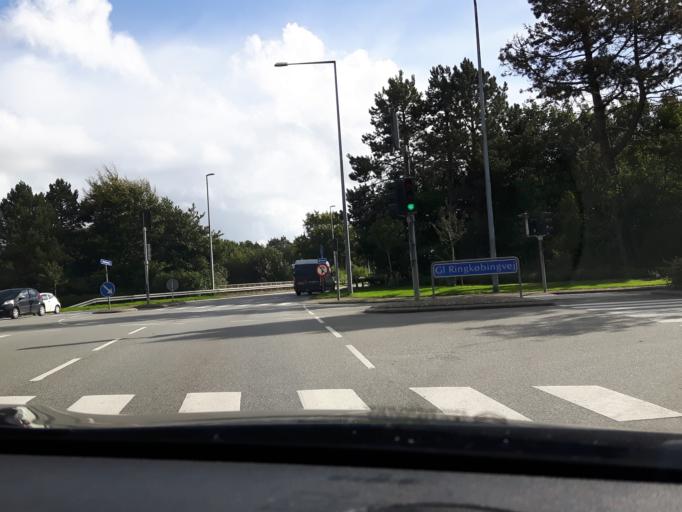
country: DK
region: Central Jutland
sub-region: Herning Kommune
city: Herning
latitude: 56.1358
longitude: 8.9493
